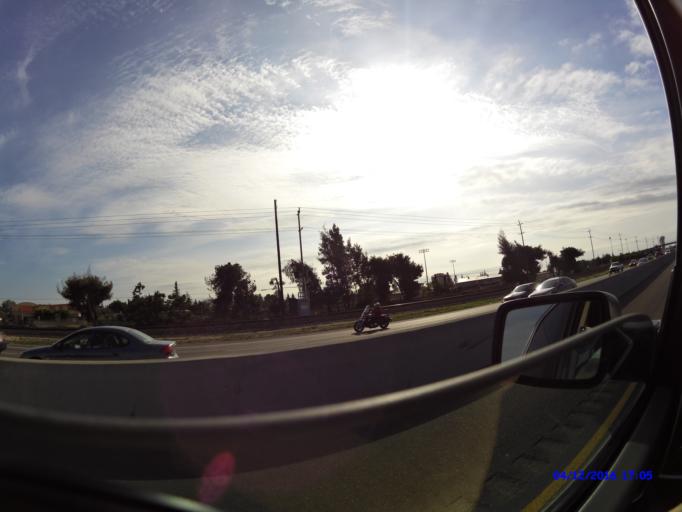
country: US
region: California
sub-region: San Joaquin County
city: Ripon
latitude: 37.7438
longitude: -121.1284
